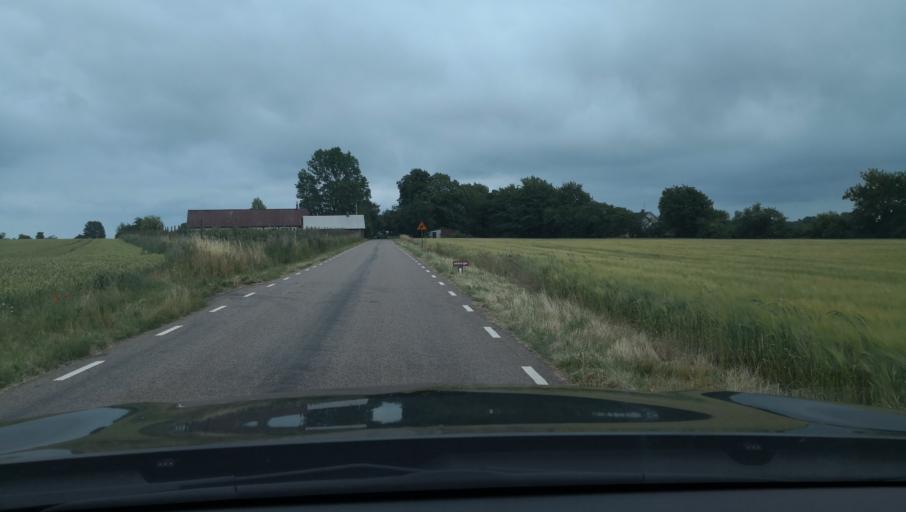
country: SE
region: Skane
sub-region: Simrishamns Kommun
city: Kivik
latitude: 55.6708
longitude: 14.2005
